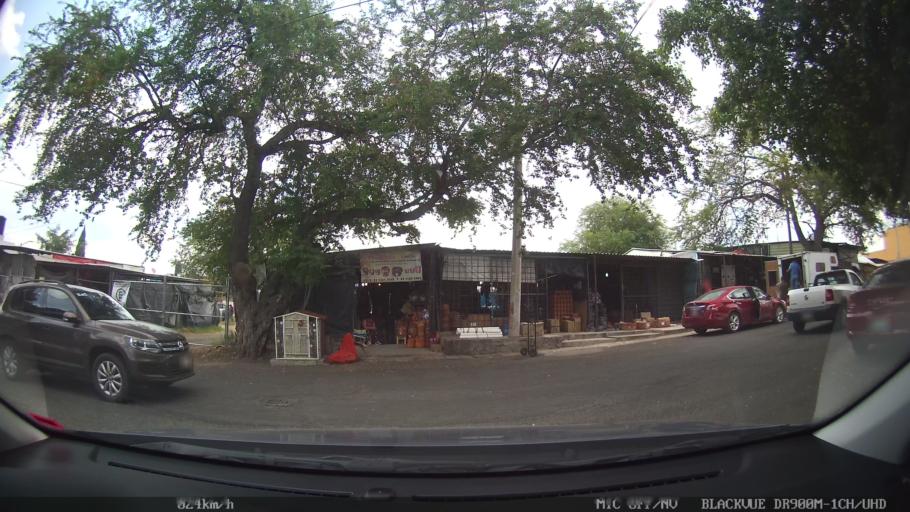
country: MX
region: Jalisco
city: Tonala
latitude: 20.6273
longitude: -103.2468
